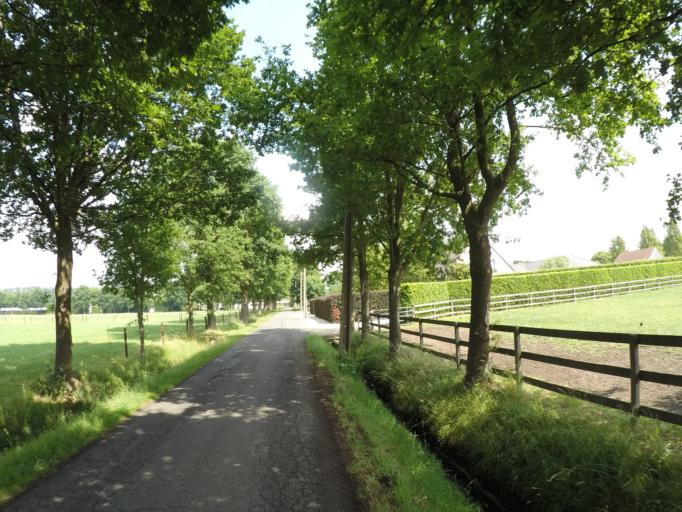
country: BE
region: Flanders
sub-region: Provincie Antwerpen
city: Brecht
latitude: 51.3454
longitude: 4.5929
